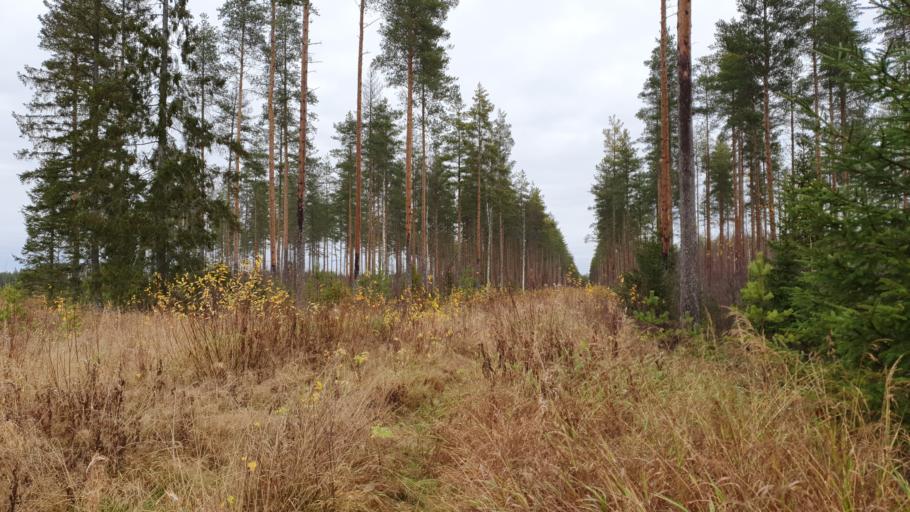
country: FI
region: Kainuu
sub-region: Kehys-Kainuu
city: Kuhmo
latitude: 64.1382
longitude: 29.4154
